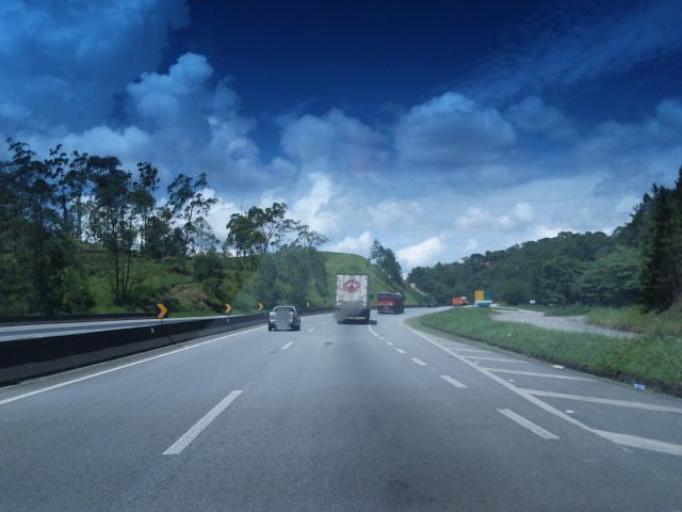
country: BR
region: Sao Paulo
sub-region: Juquitiba
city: Juquitiba
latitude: -23.9360
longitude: -47.0778
